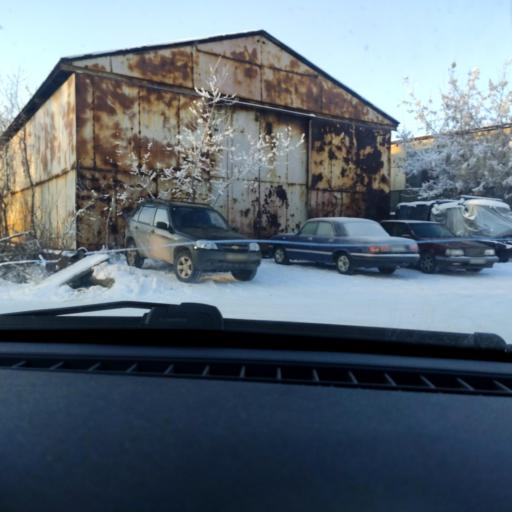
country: RU
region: Bashkortostan
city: Ufa
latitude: 54.8598
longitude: 56.0791
